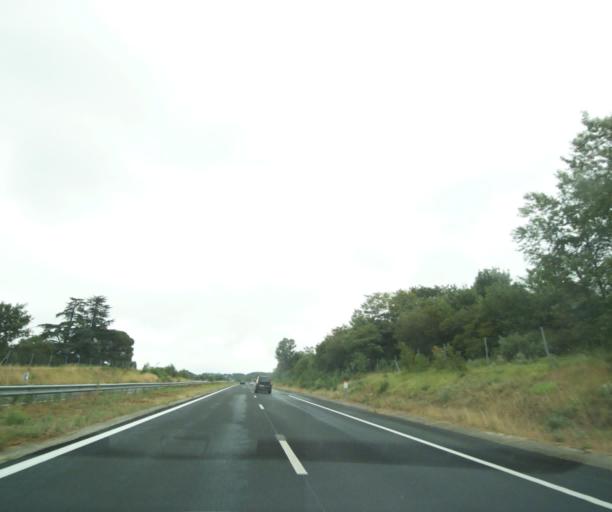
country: FR
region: Midi-Pyrenees
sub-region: Departement du Tarn
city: Lisle-sur-Tarn
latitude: 43.8130
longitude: 1.8015
